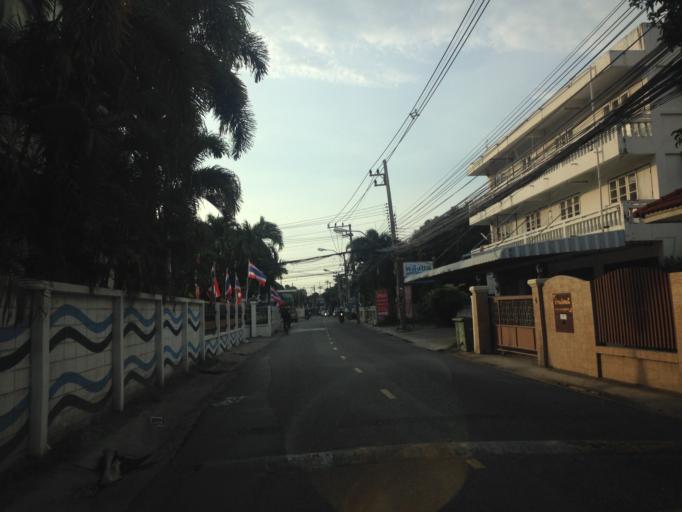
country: TH
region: Chon Buri
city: Chon Buri
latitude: 13.2792
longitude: 100.9208
